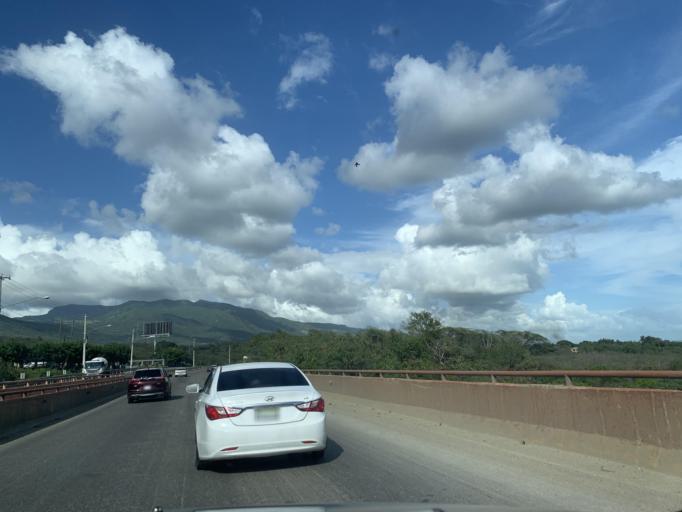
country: DO
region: Santiago
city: Villa Gonzalez
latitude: 19.5527
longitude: -70.8245
